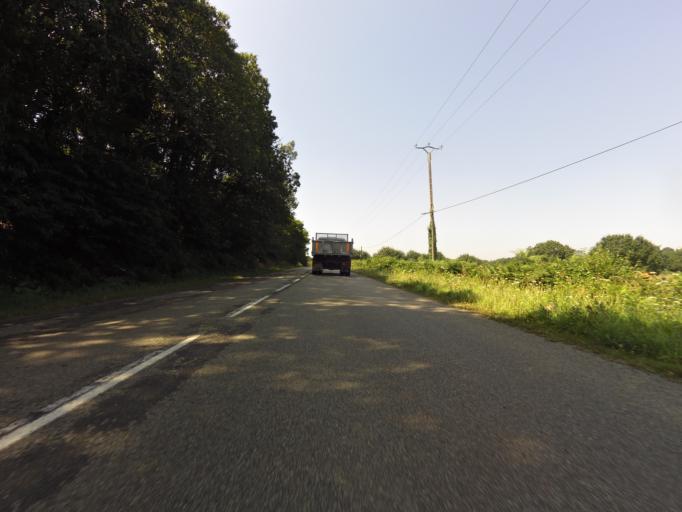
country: FR
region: Brittany
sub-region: Departement du Finistere
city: Pluguffan
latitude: 47.9459
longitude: -4.2065
